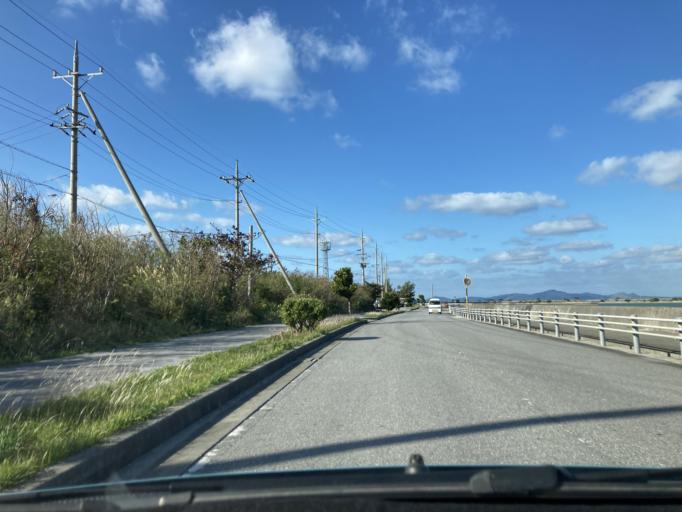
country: JP
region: Okinawa
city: Katsuren-haebaru
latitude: 26.3238
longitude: 127.9132
